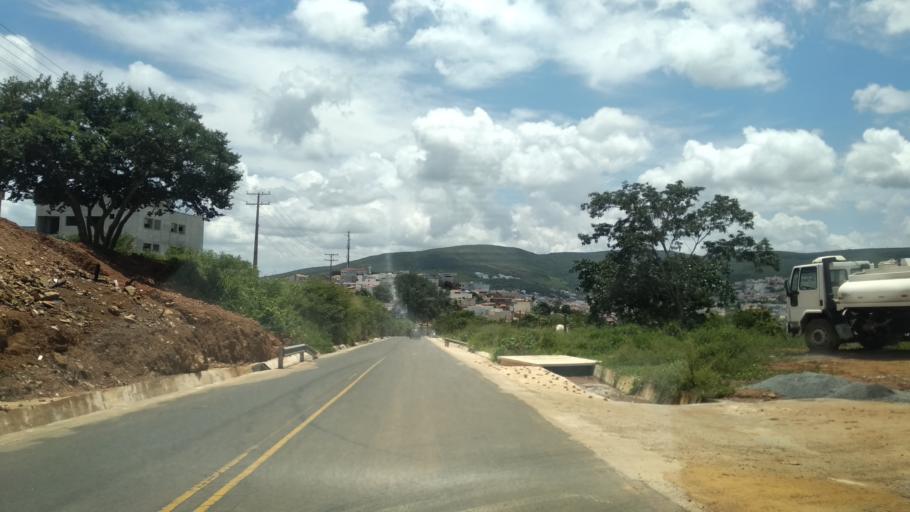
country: BR
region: Bahia
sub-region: Caetite
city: Caetite
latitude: -14.0596
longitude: -42.4914
